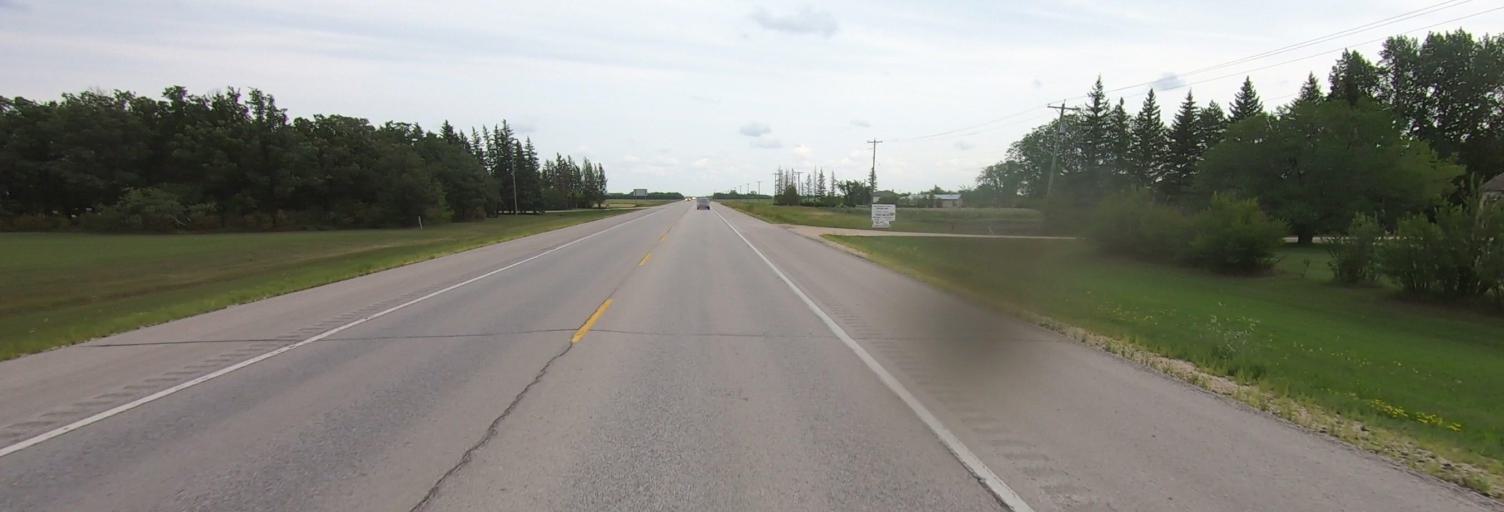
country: CA
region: Manitoba
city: Headingley
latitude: 49.7836
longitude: -97.2981
